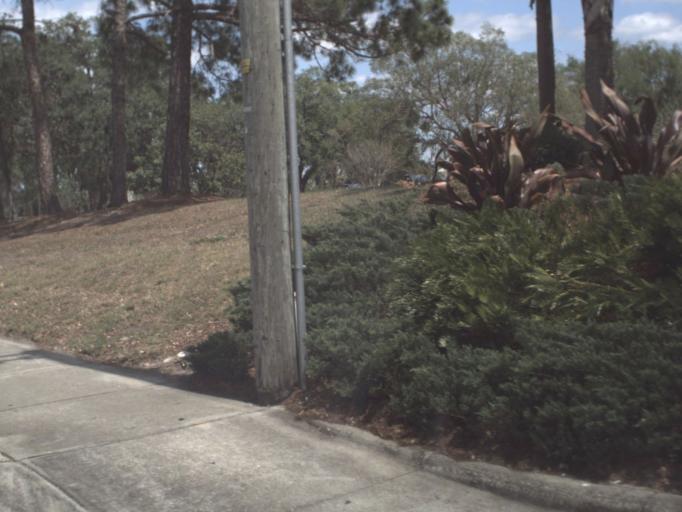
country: US
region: Florida
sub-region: Marion County
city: Ocala
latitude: 29.1587
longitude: -82.1763
